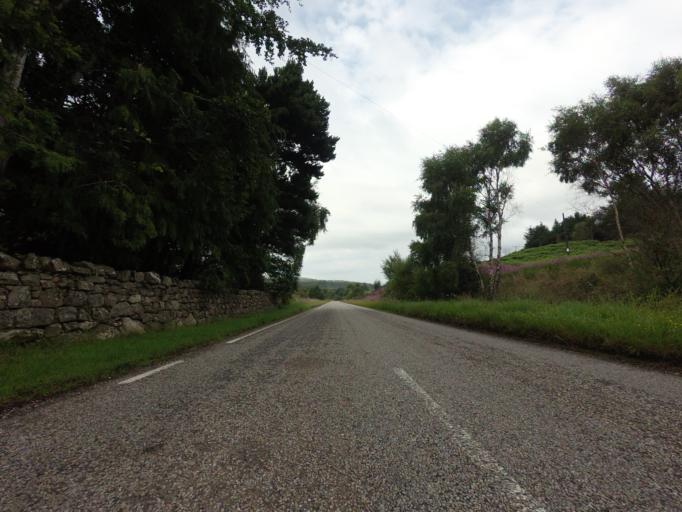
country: GB
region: Scotland
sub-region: Highland
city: Evanton
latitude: 57.9385
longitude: -4.4056
